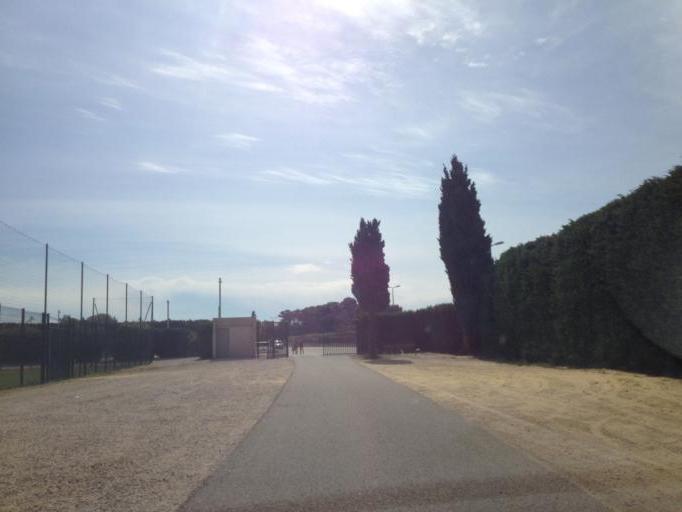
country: FR
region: Provence-Alpes-Cote d'Azur
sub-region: Departement du Vaucluse
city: Courthezon
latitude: 44.0959
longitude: 4.8827
